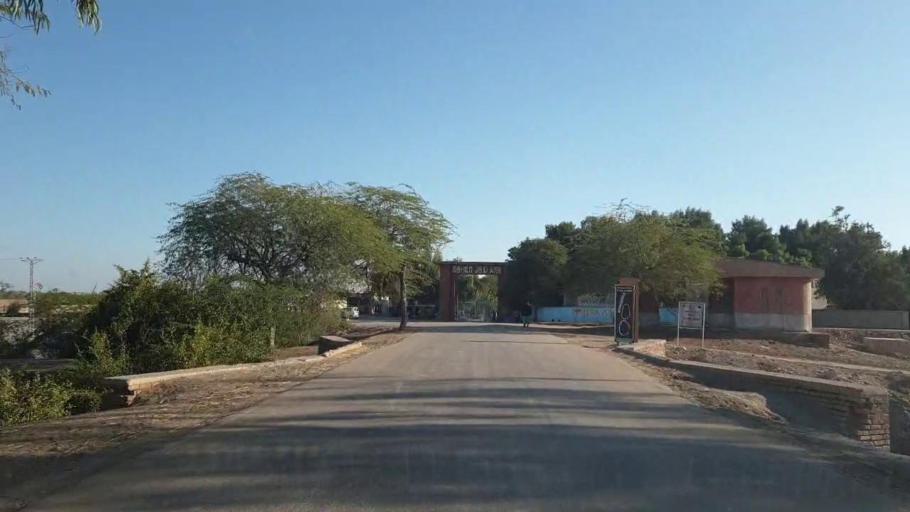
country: PK
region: Sindh
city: Dokri
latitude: 27.3303
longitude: 68.1315
